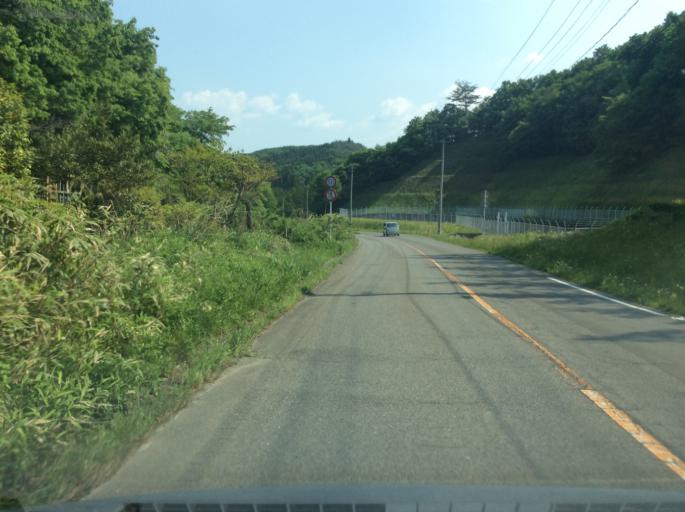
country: JP
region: Tochigi
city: Kuroiso
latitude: 37.0848
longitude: 140.2241
